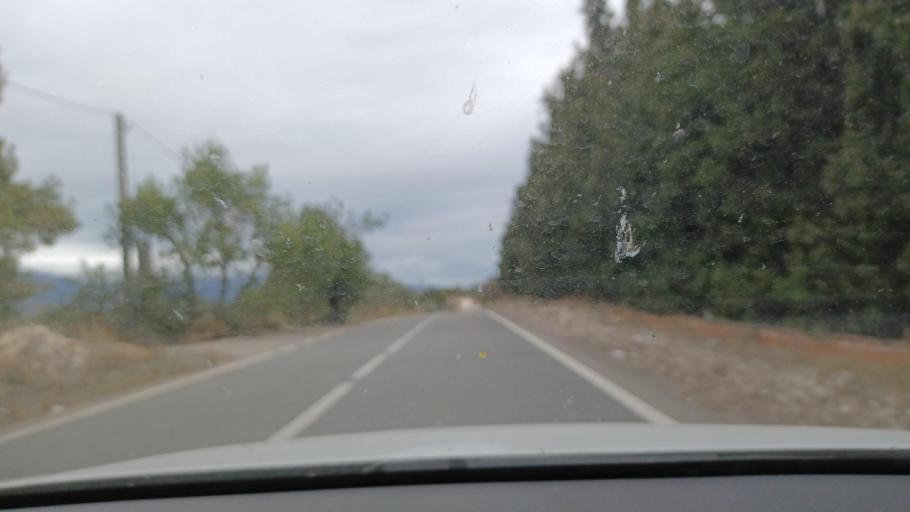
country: ES
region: Catalonia
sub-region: Provincia de Tarragona
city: Ulldecona
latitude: 40.6120
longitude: 0.3499
